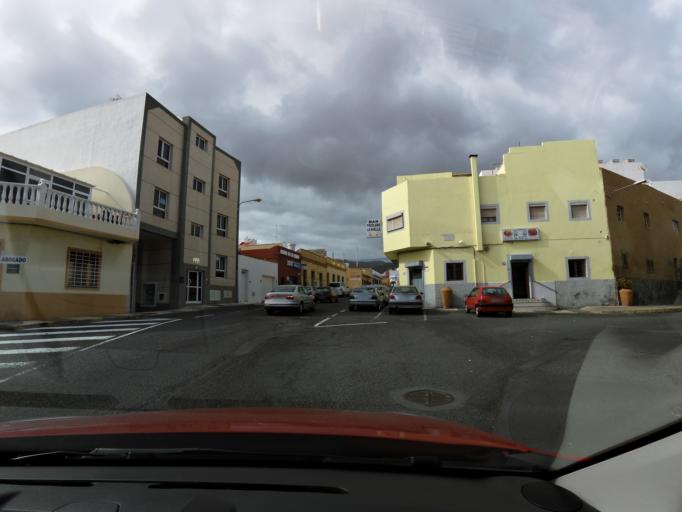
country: ES
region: Canary Islands
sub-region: Provincia de Las Palmas
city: Ingenio
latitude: 27.9183
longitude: -15.4332
